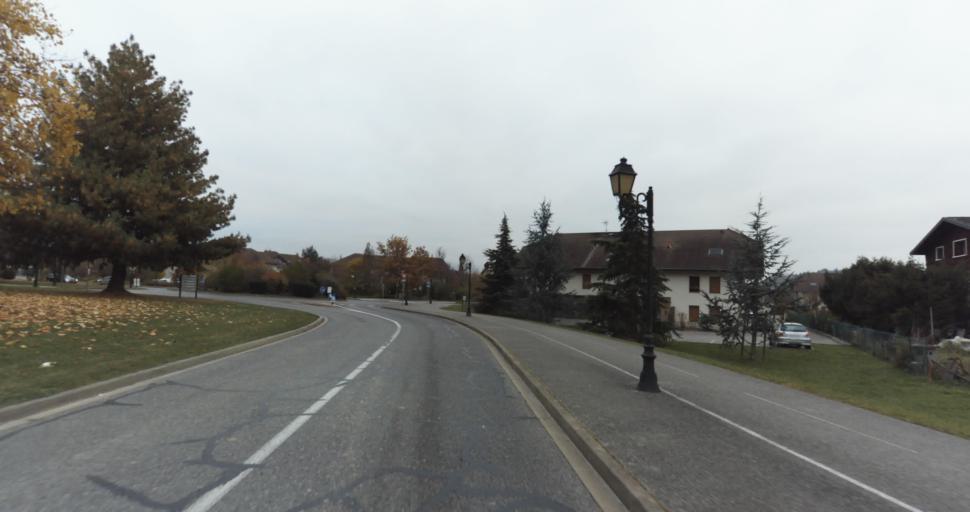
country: FR
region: Rhone-Alpes
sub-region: Departement de la Haute-Savoie
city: Epagny
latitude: 45.9405
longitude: 6.0902
